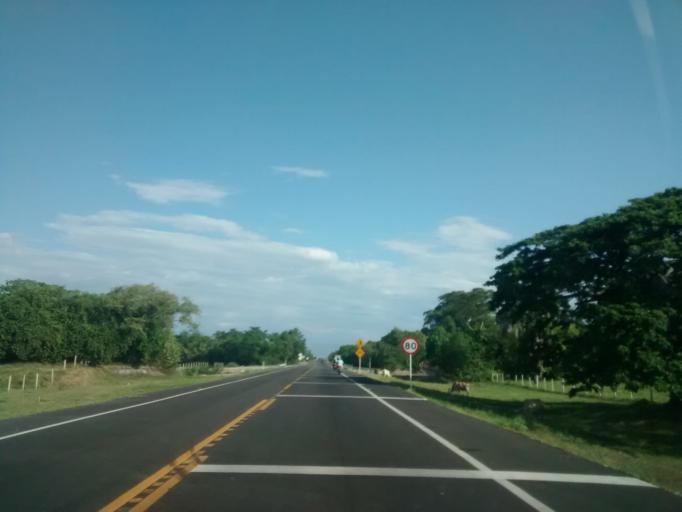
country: CO
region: Tolima
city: Espinal
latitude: 4.1609
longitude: -74.9183
